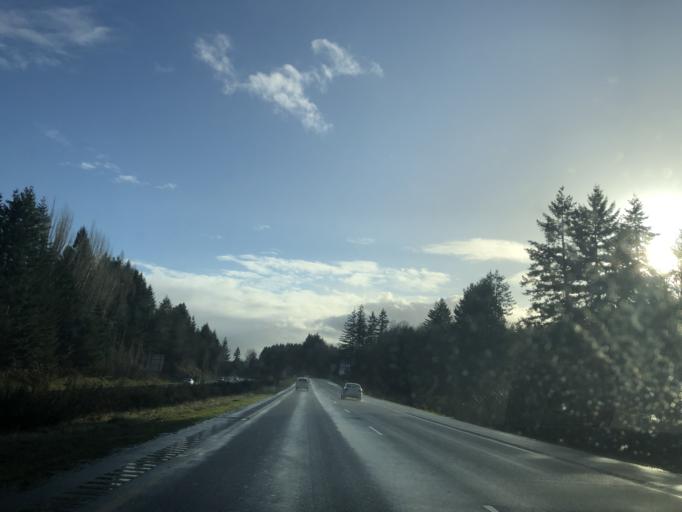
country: US
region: Washington
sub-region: Kitsap County
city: Silverdale
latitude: 47.6525
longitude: -122.7061
